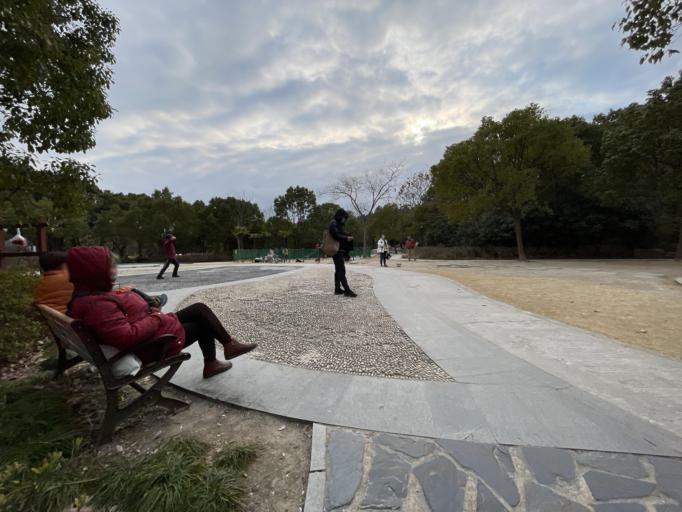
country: CN
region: Shanghai Shi
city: Yangpu
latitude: 31.2952
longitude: 121.5239
